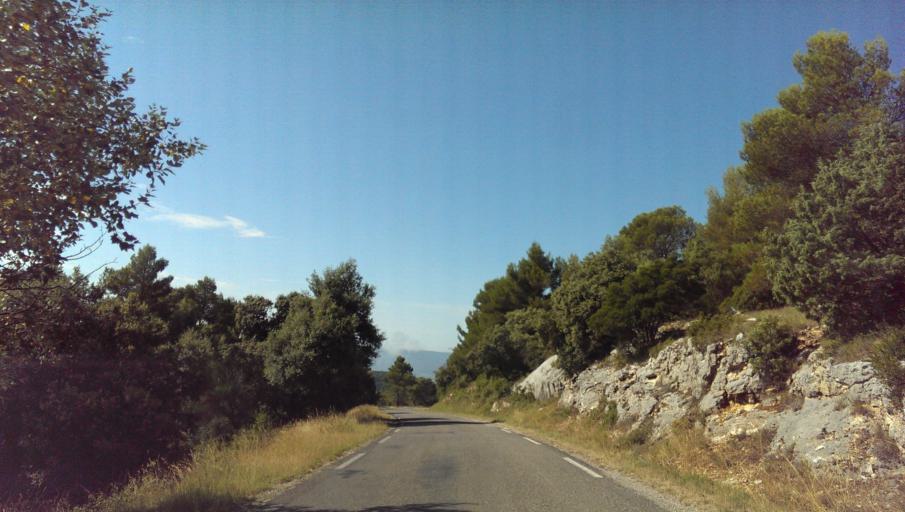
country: FR
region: Provence-Alpes-Cote d'Azur
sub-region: Departement du Vaucluse
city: Gordes
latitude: 43.9482
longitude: 5.1954
